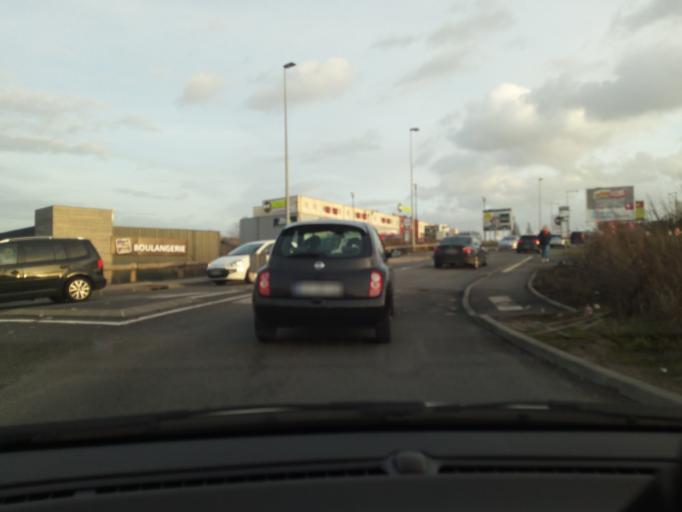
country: FR
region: Nord-Pas-de-Calais
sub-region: Departement du Nord
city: Hautmont
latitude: 50.2522
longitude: 3.9406
